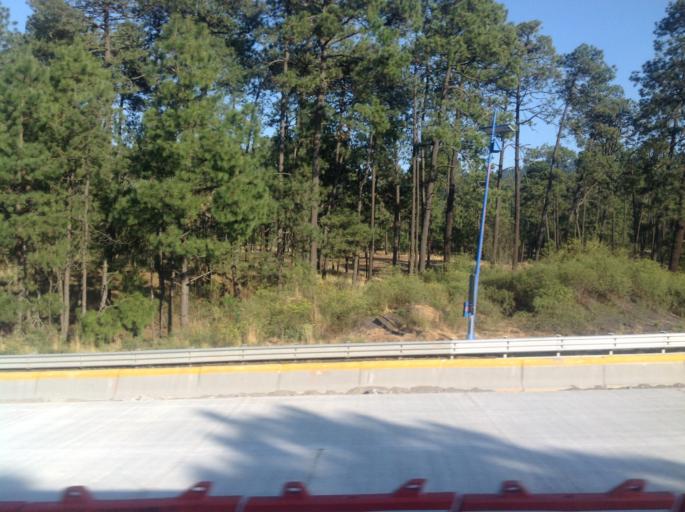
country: MX
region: Mexico
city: Rio Frio de Juarez
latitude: 19.3360
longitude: -98.6828
